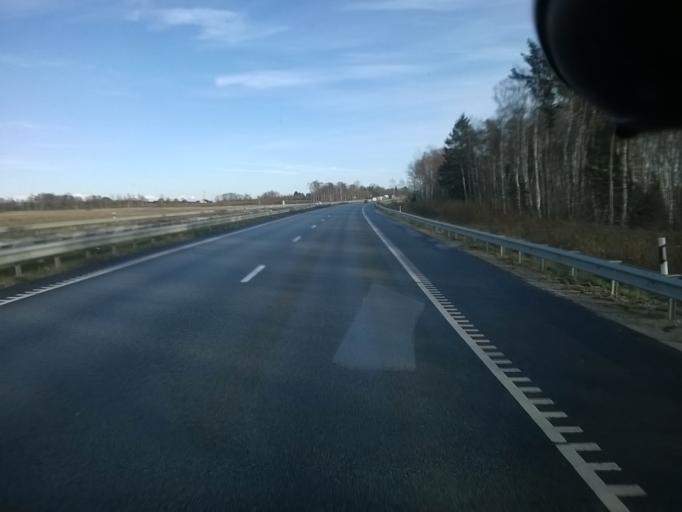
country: EE
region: Harju
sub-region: Kiili vald
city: Kiili
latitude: 59.3318
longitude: 24.7968
